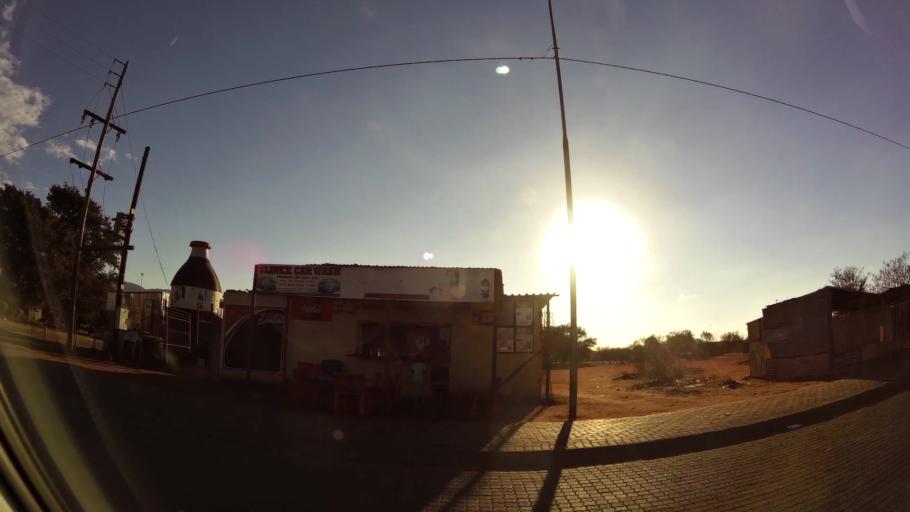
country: ZA
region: Limpopo
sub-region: Waterberg District Municipality
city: Mokopane
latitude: -24.1561
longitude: 28.9889
